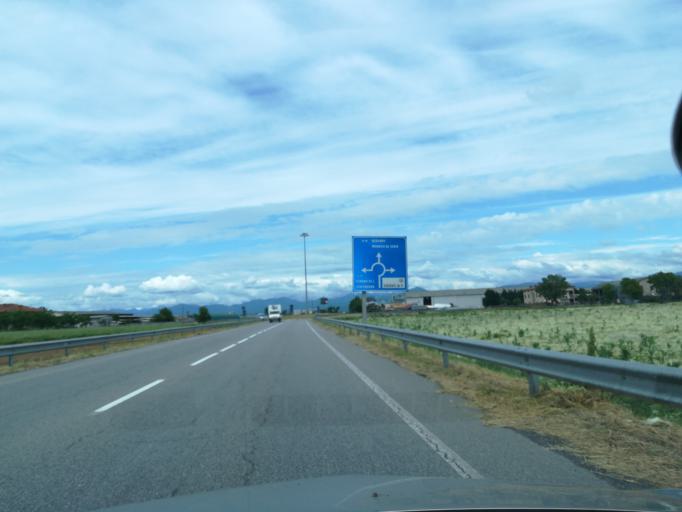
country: IT
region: Lombardy
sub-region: Provincia di Bergamo
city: Cividate al Piano
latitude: 45.5466
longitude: 9.8236
